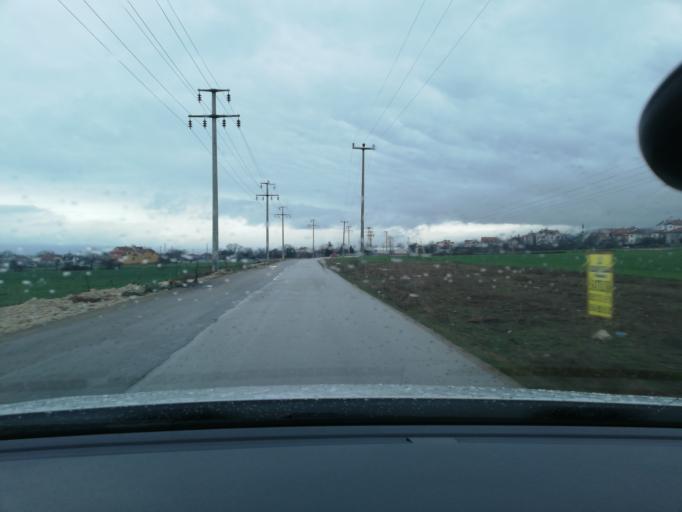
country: TR
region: Bolu
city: Bolu
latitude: 40.7571
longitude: 31.6388
